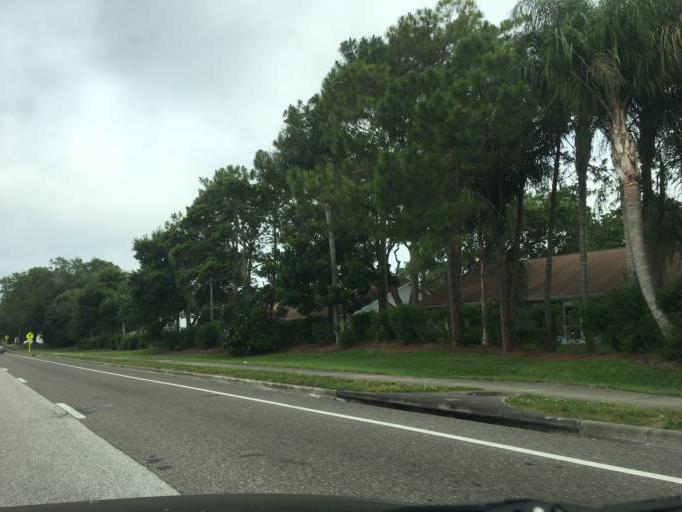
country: US
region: Florida
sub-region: Pinellas County
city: Dunedin
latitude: 27.9993
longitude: -82.7632
